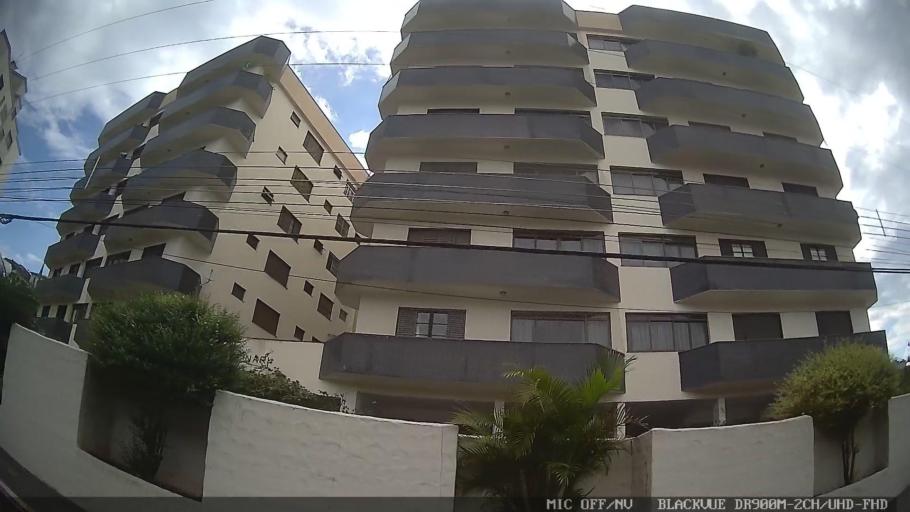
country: BR
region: Sao Paulo
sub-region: Serra Negra
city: Serra Negra
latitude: -22.6066
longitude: -46.7058
